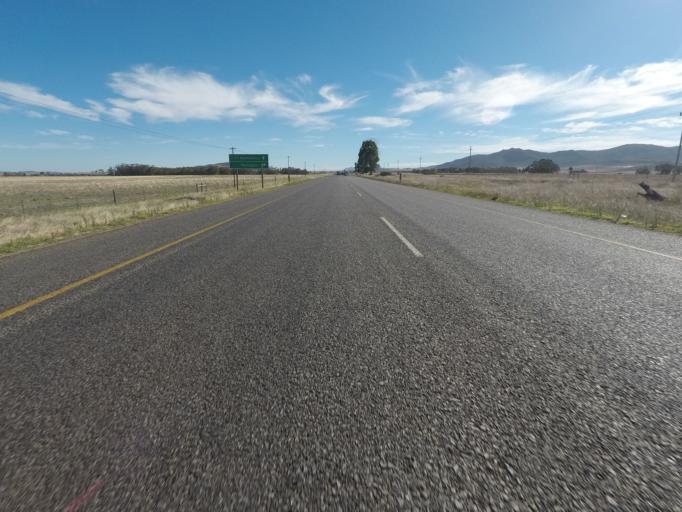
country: ZA
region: Western Cape
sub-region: West Coast District Municipality
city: Malmesbury
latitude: -33.6242
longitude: 18.7247
